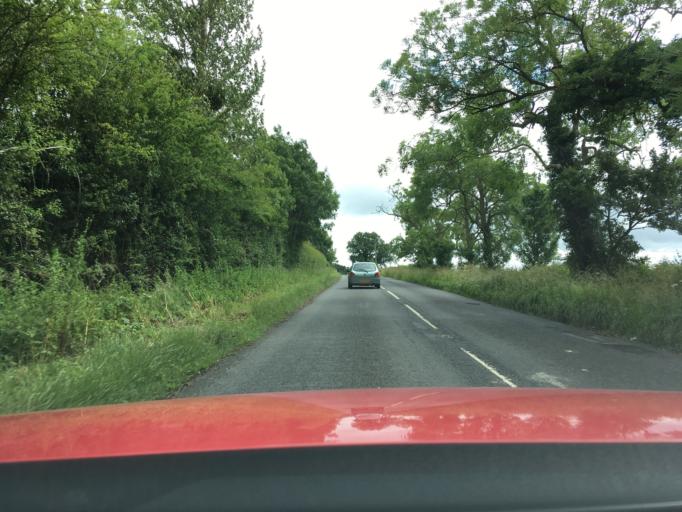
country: GB
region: England
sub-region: Gloucestershire
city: Winchcombe
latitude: 51.9762
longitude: -1.9724
